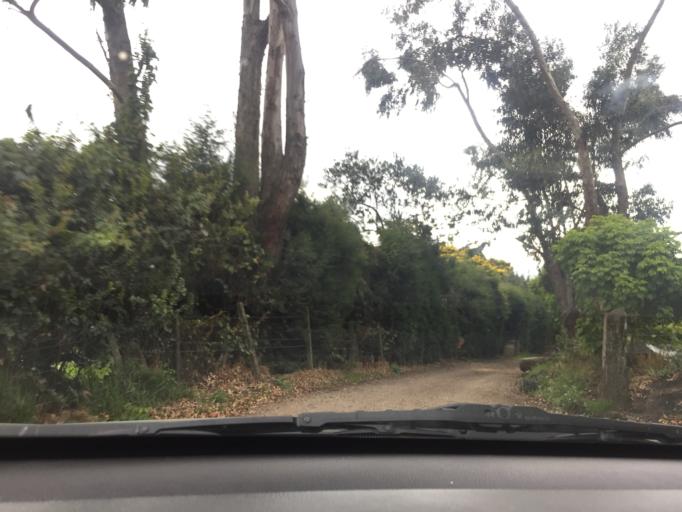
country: CO
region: Cundinamarca
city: Tabio
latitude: 4.9396
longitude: -74.1285
